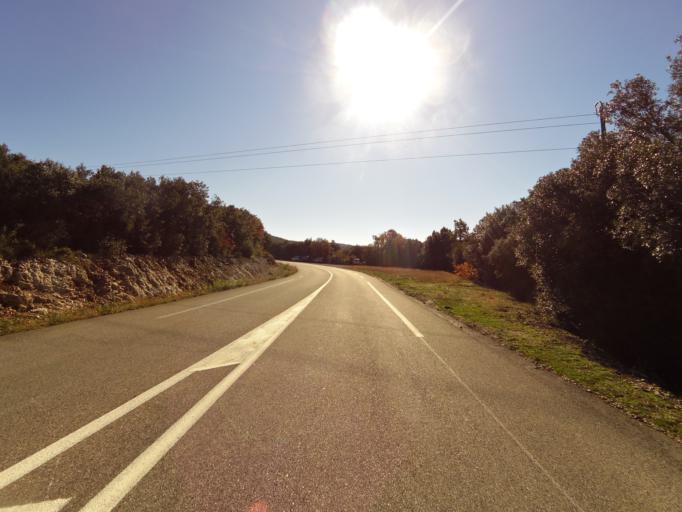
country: FR
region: Rhone-Alpes
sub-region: Departement de l'Ardeche
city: Ruoms
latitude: 44.4050
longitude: 4.4266
